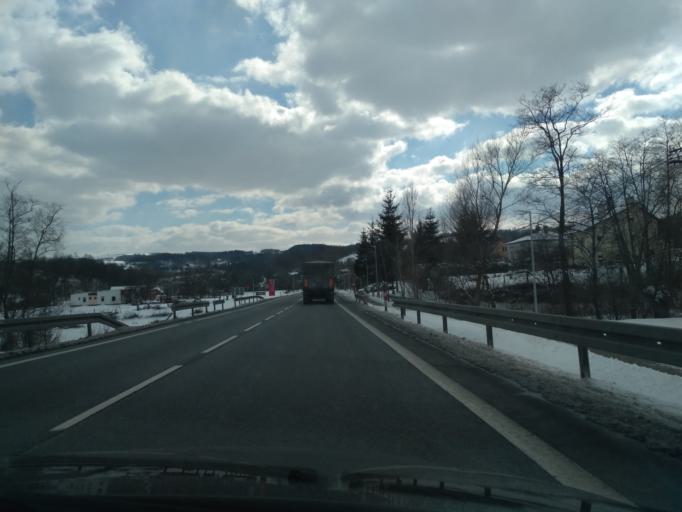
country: PL
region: Subcarpathian Voivodeship
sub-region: Powiat strzyzowski
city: Babica
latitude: 49.9137
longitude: 21.8683
